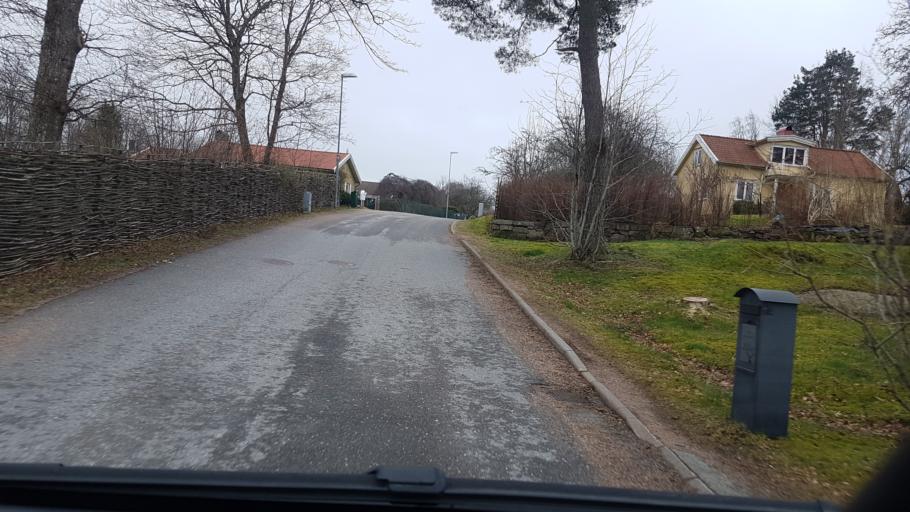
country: SE
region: Vaestra Goetaland
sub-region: Lerums Kommun
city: Lerum
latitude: 57.7679
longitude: 12.2796
